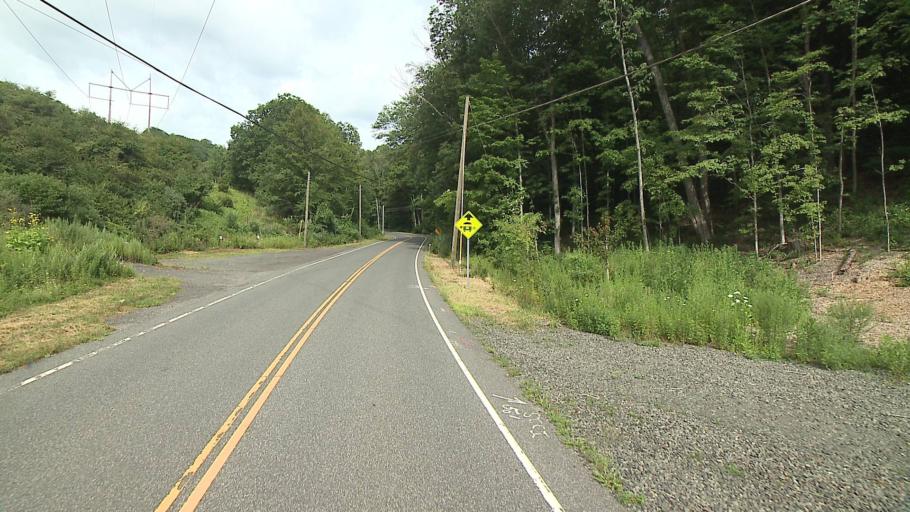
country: US
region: Connecticut
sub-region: Litchfield County
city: Bethlehem Village
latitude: 41.5989
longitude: -73.2735
